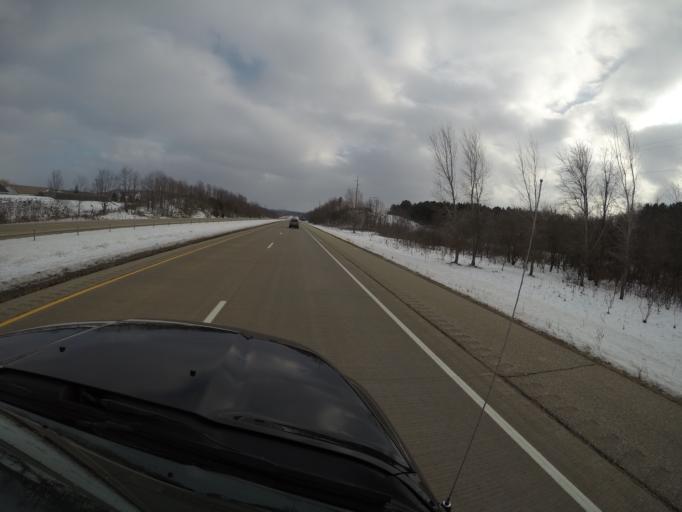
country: US
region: Wisconsin
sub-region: La Crosse County
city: Holmen
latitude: 43.9519
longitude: -91.2746
